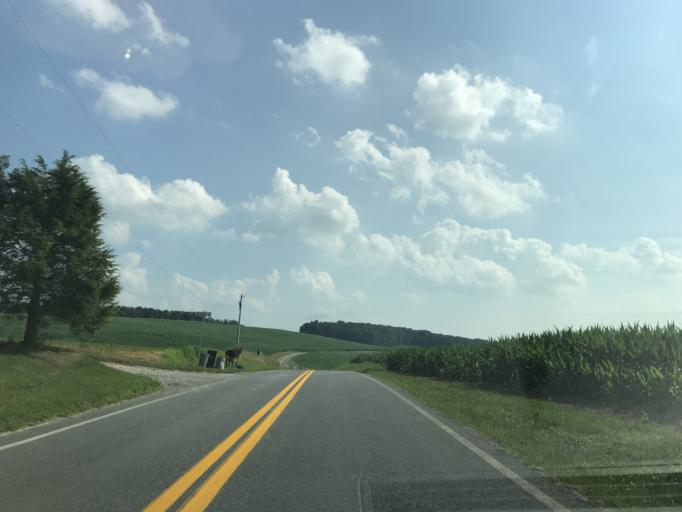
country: US
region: Maryland
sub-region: Carroll County
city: Manchester
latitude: 39.6441
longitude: -76.9386
